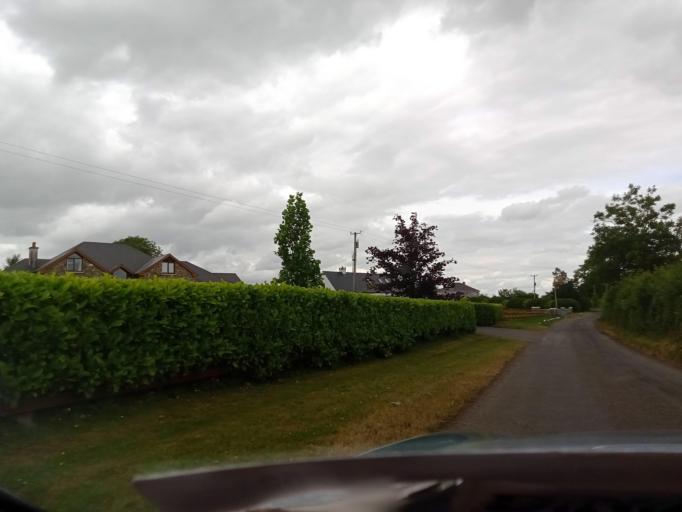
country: IE
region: Leinster
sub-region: Kilkenny
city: Thomastown
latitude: 52.5561
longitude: -7.2078
